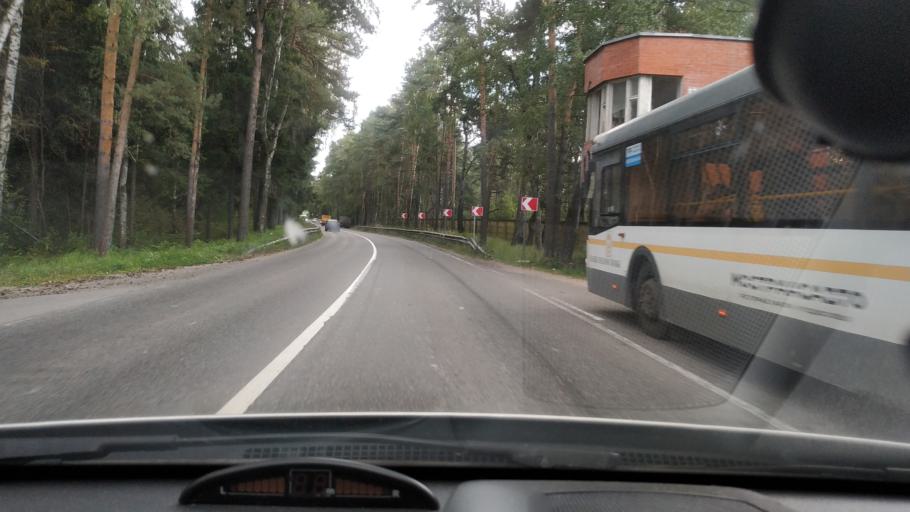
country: RU
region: Moskovskaya
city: Chornaya
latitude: 55.7777
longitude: 38.0461
